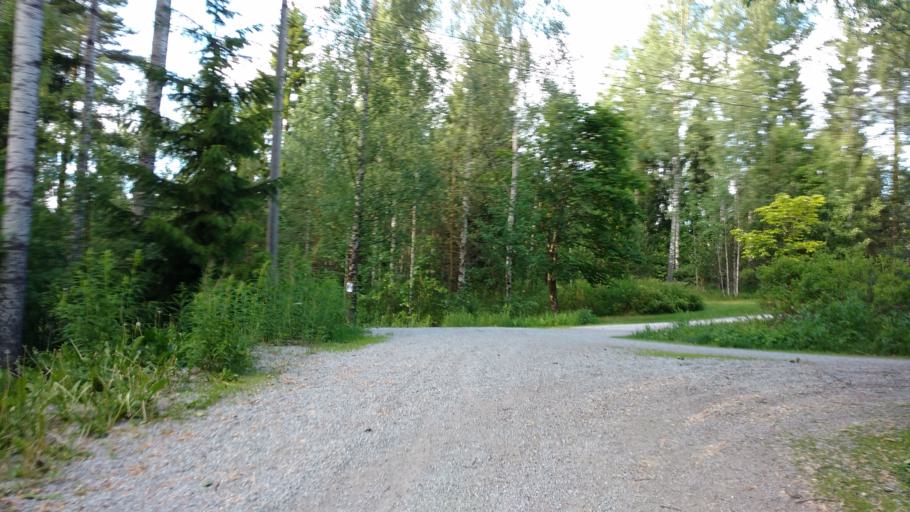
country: FI
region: Varsinais-Suomi
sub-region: Salo
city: Salo
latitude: 60.3909
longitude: 23.1757
